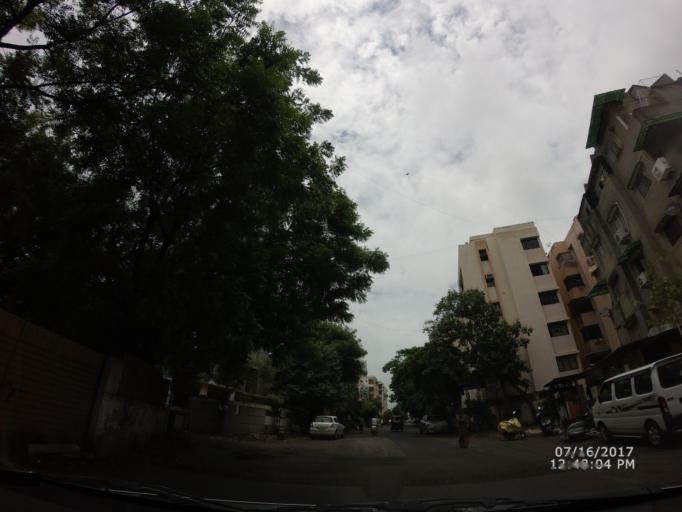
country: IN
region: Gujarat
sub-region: Ahmadabad
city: Sarkhej
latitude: 23.0183
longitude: 72.5114
